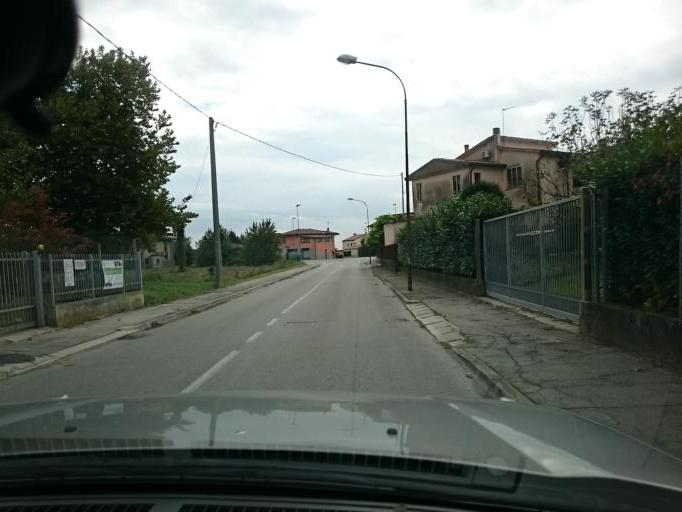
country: IT
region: Veneto
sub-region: Provincia di Padova
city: Vallonga
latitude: 45.2707
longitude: 12.0817
